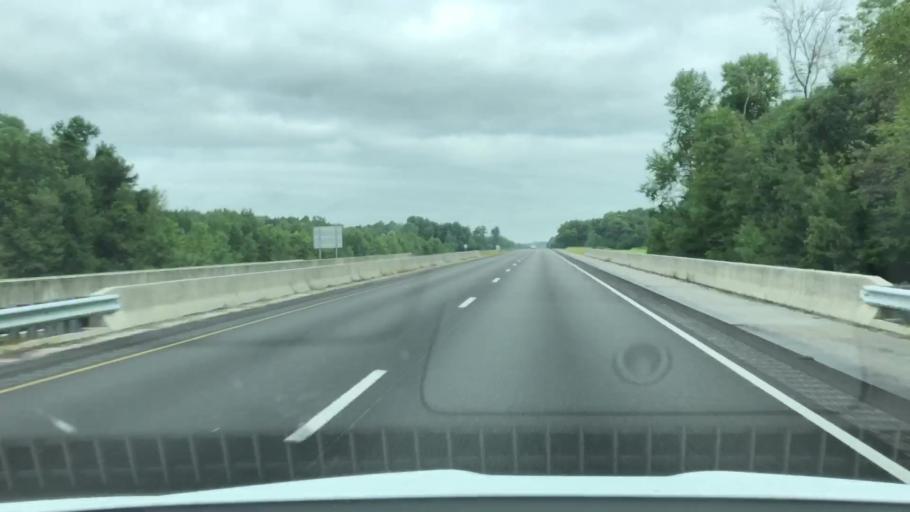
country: US
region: North Carolina
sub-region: Wayne County
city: Fremont
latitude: 35.5611
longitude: -77.9876
